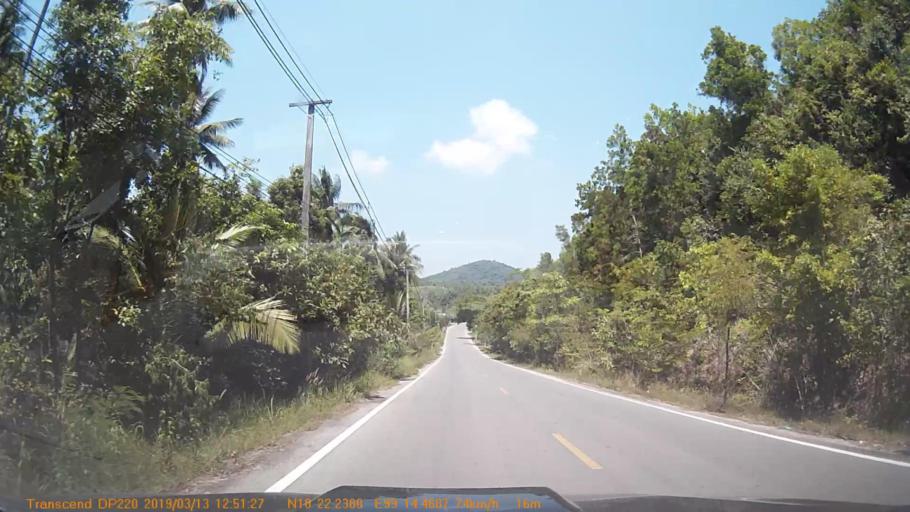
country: TH
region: Chumphon
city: Chumphon
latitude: 10.3709
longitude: 99.2412
